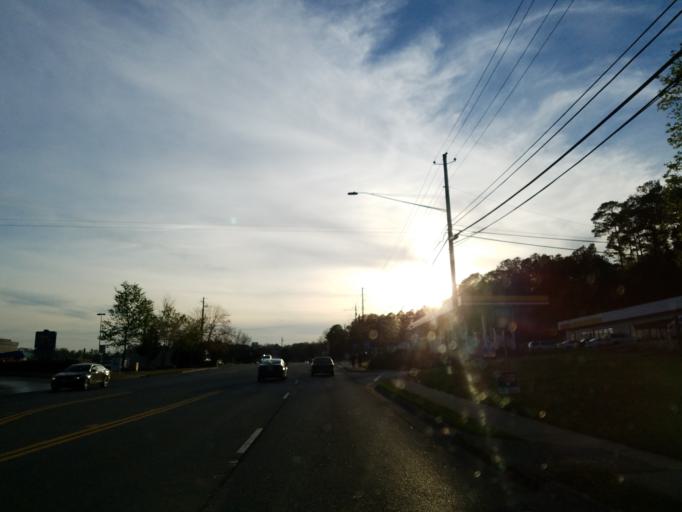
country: US
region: Georgia
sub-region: Cherokee County
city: Canton
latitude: 34.2446
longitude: -84.4876
